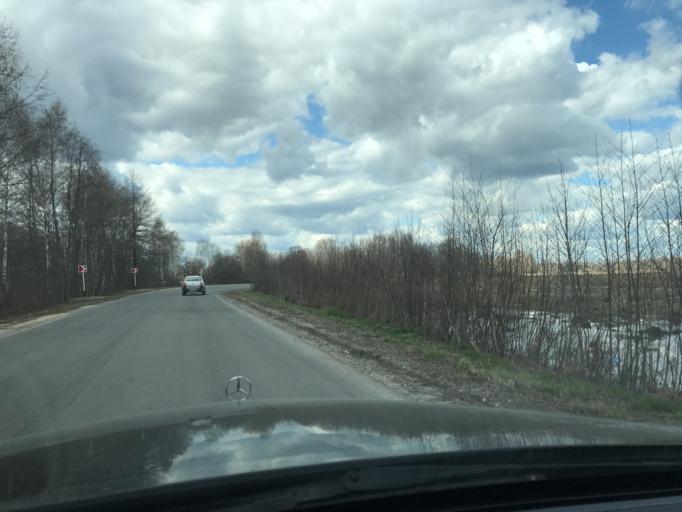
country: RU
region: Vladimir
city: Pokrov
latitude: 55.8882
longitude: 39.2295
